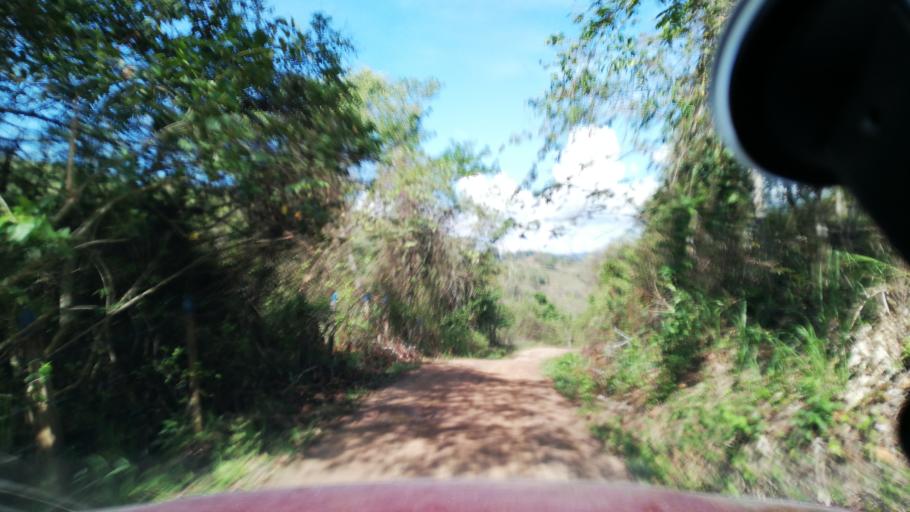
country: CO
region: Cundinamarca
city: Quipile
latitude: 4.7480
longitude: -74.6128
